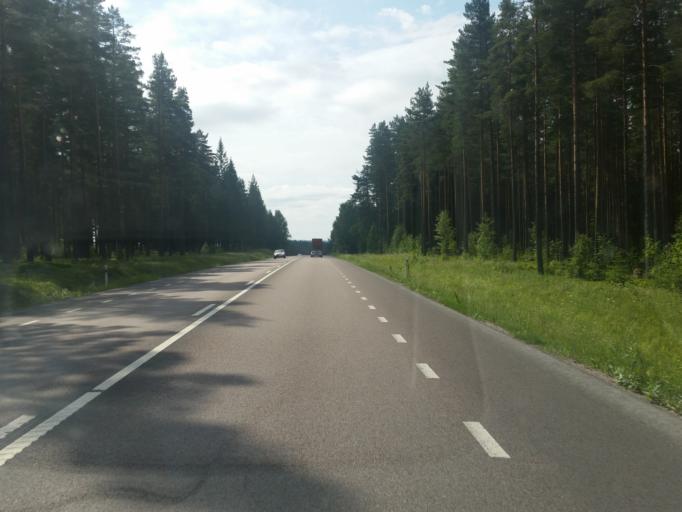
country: SE
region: Dalarna
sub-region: Gagnefs Kommun
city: Gagnef
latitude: 60.6403
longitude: 15.0577
